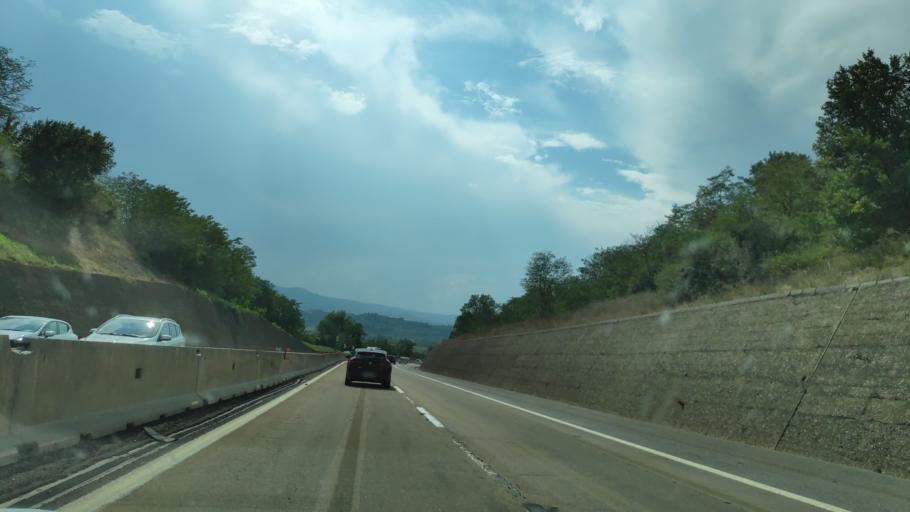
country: IT
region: Tuscany
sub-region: Province of Arezzo
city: Montalto
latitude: 43.5148
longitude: 11.6307
